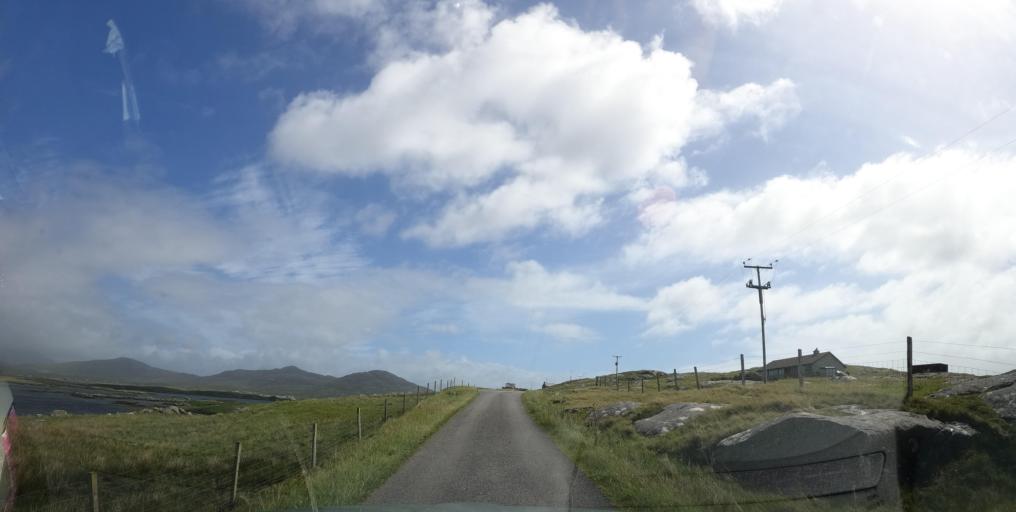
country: GB
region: Scotland
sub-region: Eilean Siar
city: Isle of South Uist
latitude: 57.1359
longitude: -7.3319
